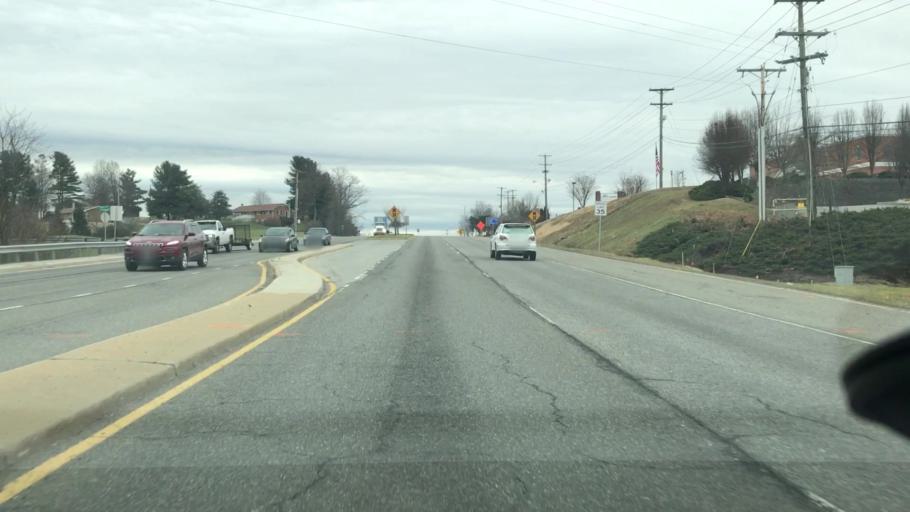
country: US
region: Virginia
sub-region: Montgomery County
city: Christiansburg
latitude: 37.1485
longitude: -80.4149
